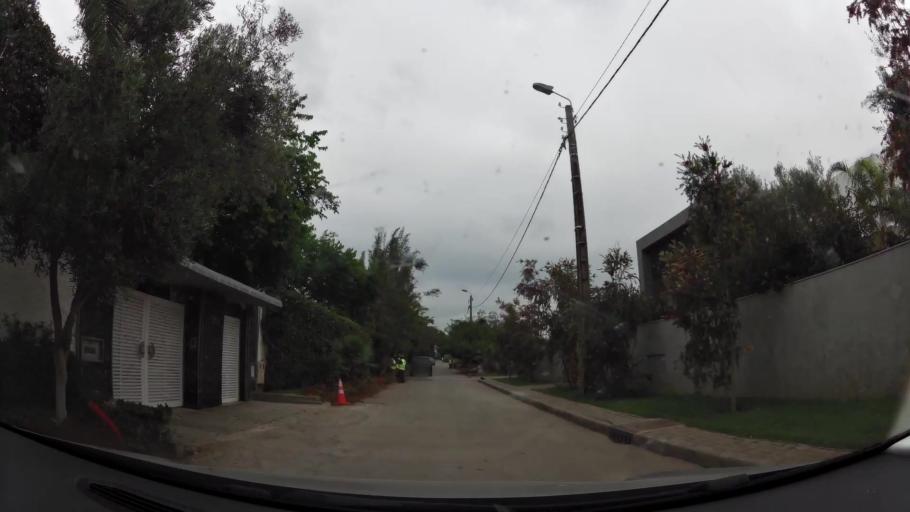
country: MA
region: Rabat-Sale-Zemmour-Zaer
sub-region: Rabat
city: Rabat
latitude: 33.9621
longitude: -6.8164
